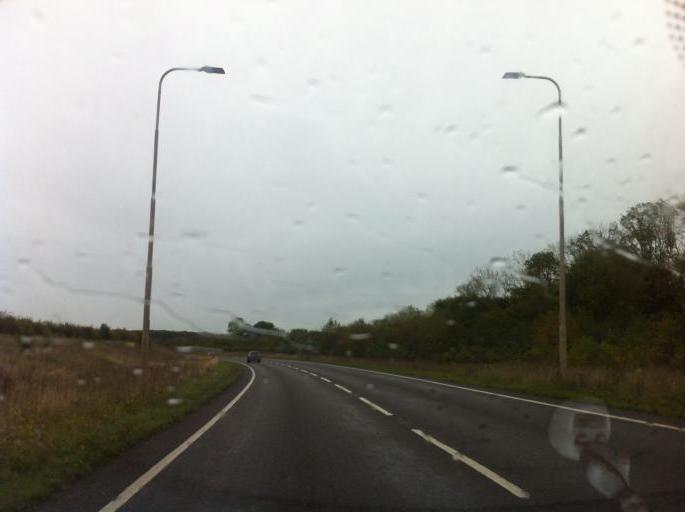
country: GB
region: England
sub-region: Peterborough
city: Eye
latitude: 52.6079
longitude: -0.2183
